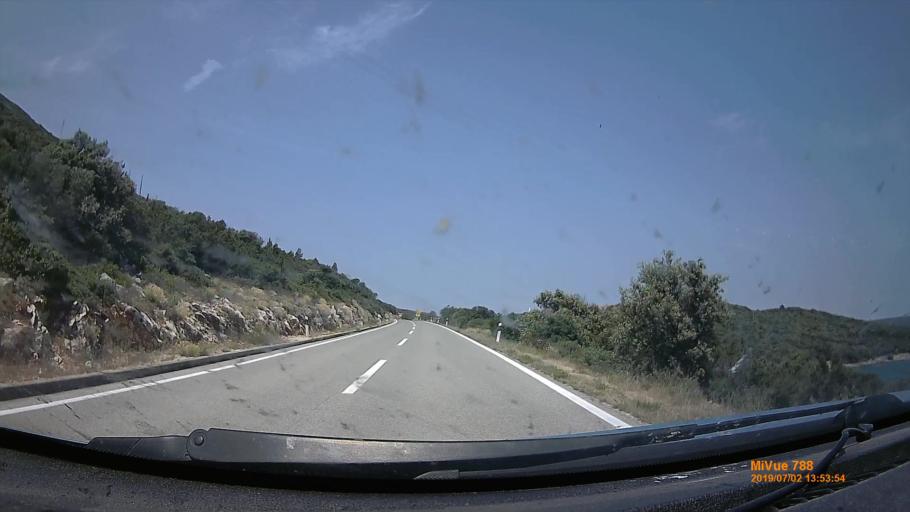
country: HR
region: Primorsko-Goranska
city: Mali Losinj
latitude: 44.6325
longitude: 14.3924
